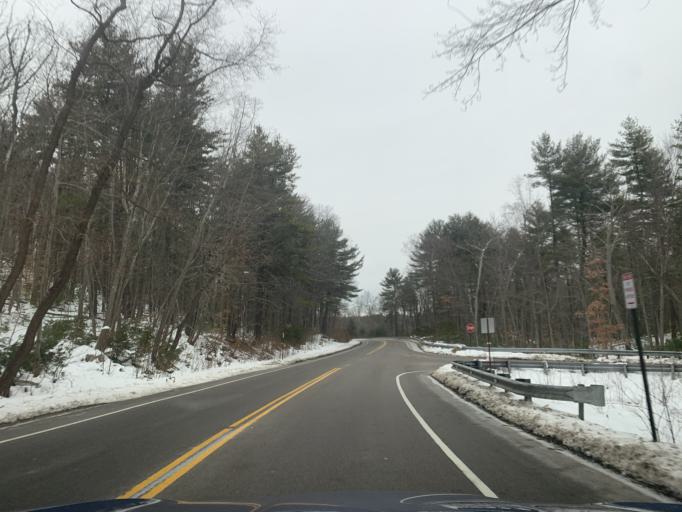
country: US
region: Massachusetts
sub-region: Norfolk County
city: Milton
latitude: 42.2189
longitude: -71.0916
